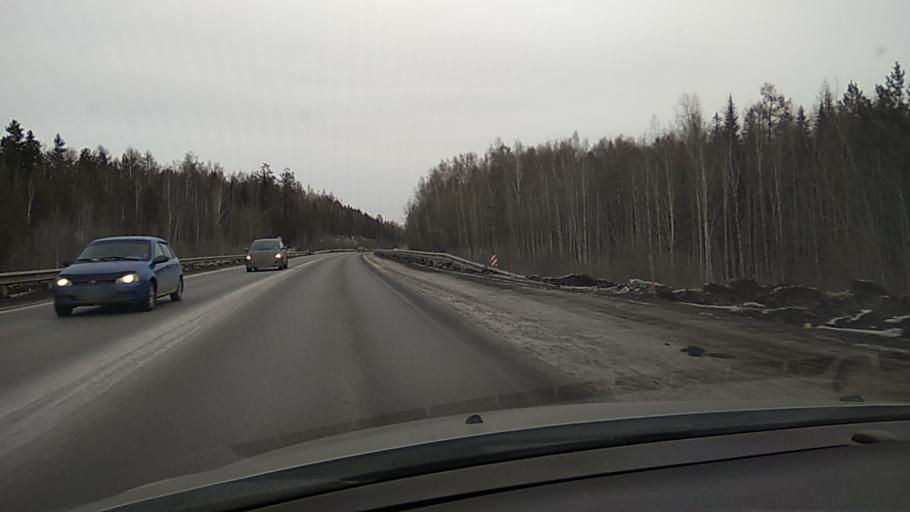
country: RU
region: Sverdlovsk
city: Talitsa
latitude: 56.8369
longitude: 60.0010
